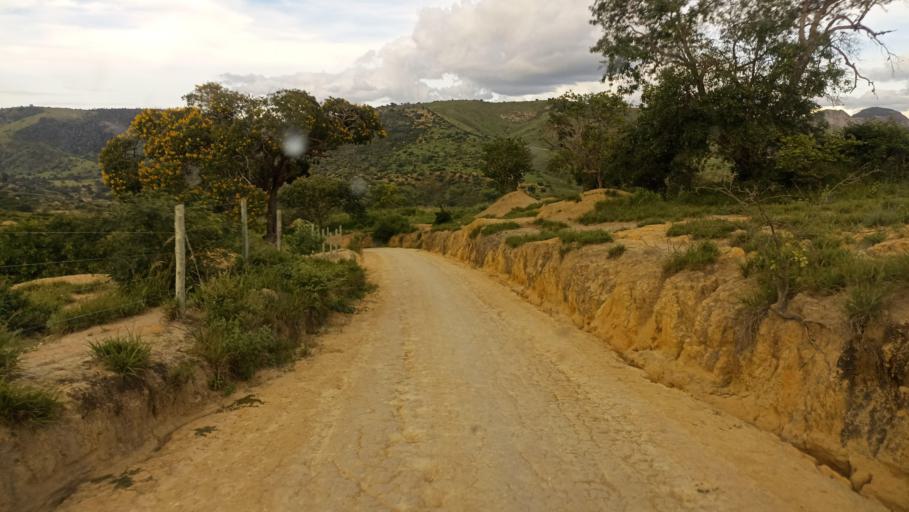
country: BR
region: Minas Gerais
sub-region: Almenara
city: Almenara
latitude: -16.5413
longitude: -40.4457
